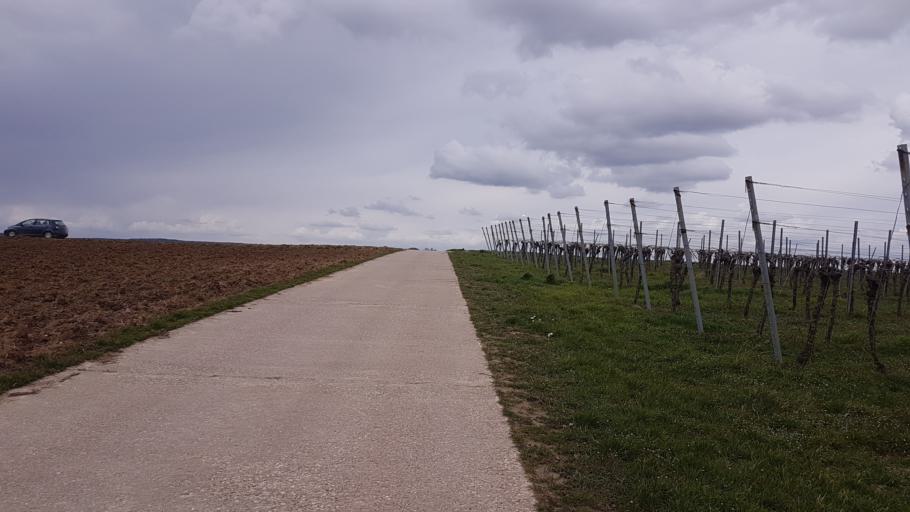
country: DE
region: Baden-Wuerttemberg
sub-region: Regierungsbezirk Stuttgart
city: Lauffen am Neckar
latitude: 49.0805
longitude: 9.1339
